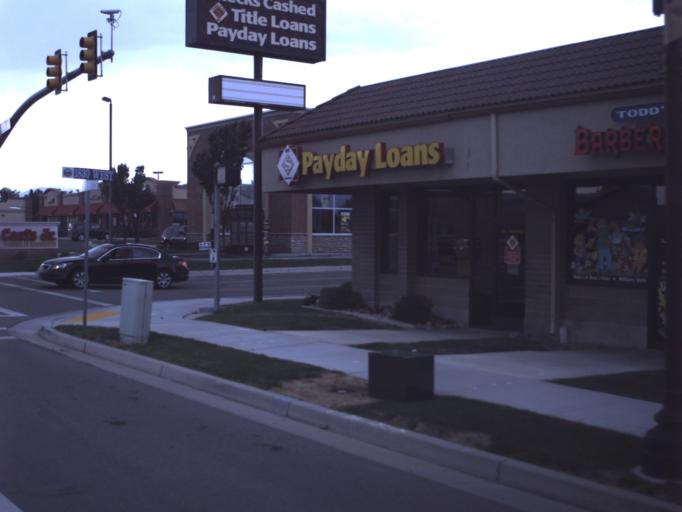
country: US
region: Utah
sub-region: Salt Lake County
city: Riverton
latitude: 40.5224
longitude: -111.9409
